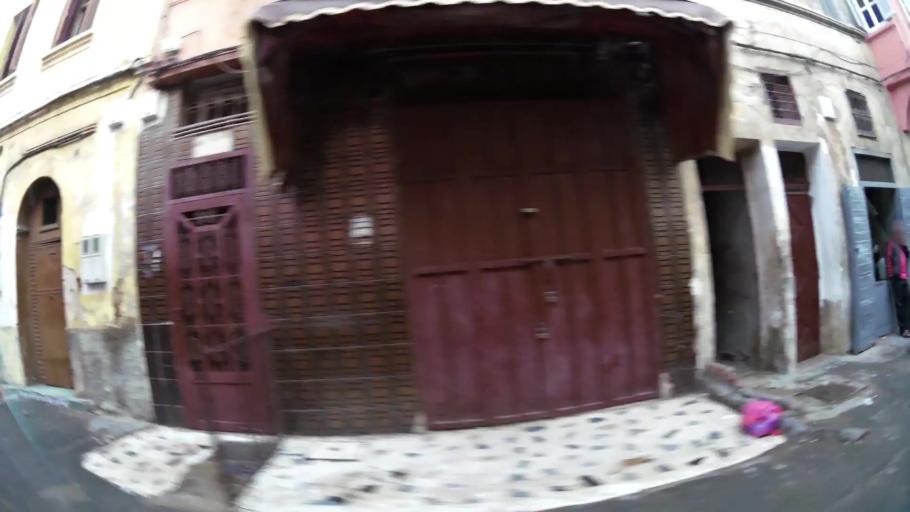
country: MA
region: Grand Casablanca
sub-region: Casablanca
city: Casablanca
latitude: 33.5773
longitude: -7.6022
